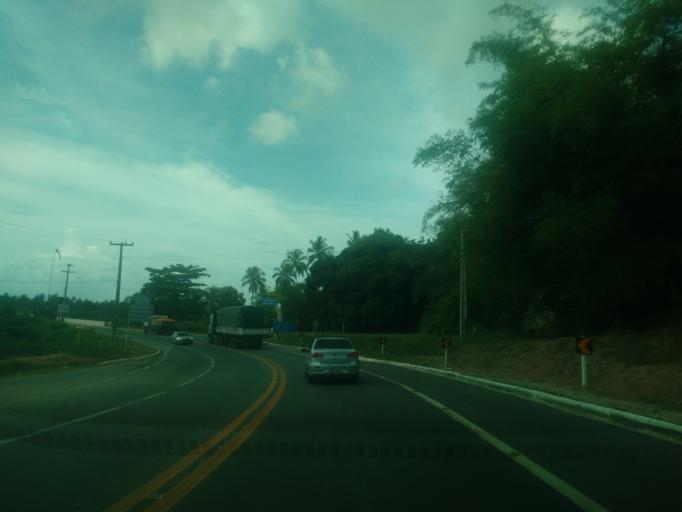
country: BR
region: Alagoas
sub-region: Marechal Deodoro
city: Marechal Deodoro
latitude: -9.6927
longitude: -35.8166
